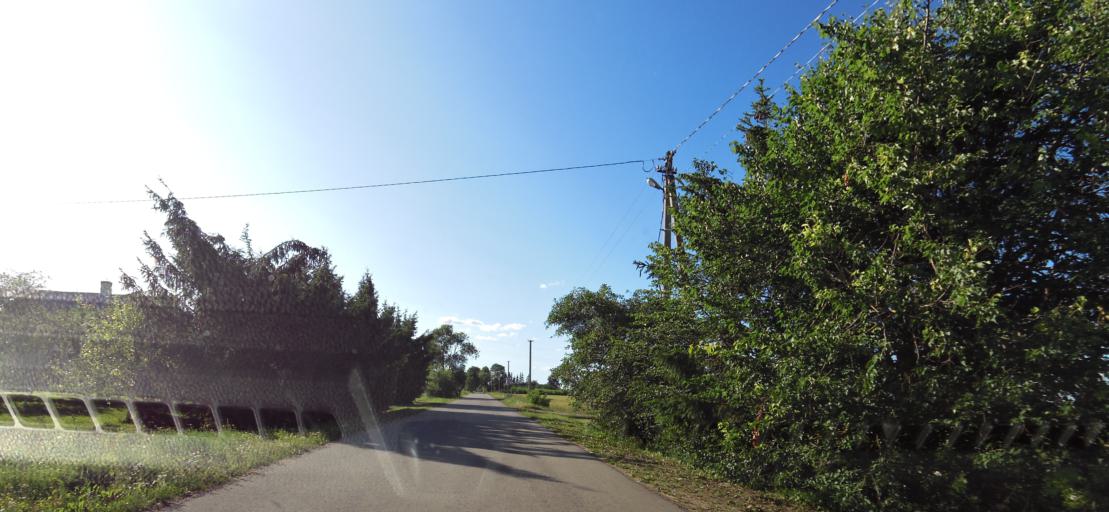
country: LT
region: Panevezys
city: Pasvalys
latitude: 56.1358
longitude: 24.5367
